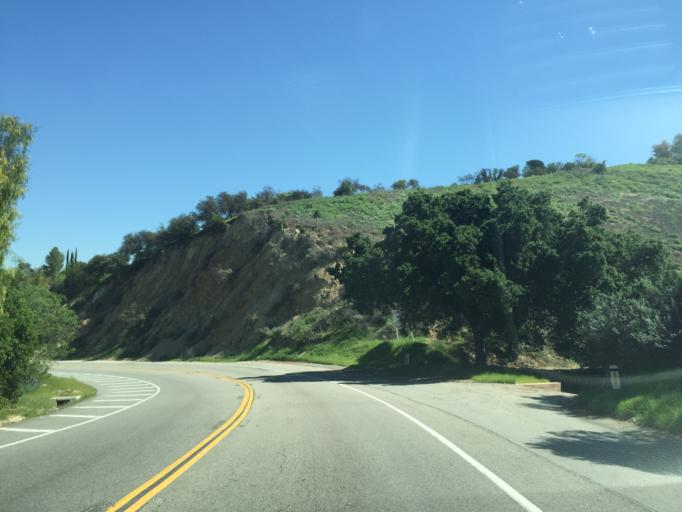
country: US
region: California
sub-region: Los Angeles County
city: Woodland Hills
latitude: 34.1457
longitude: -118.6062
